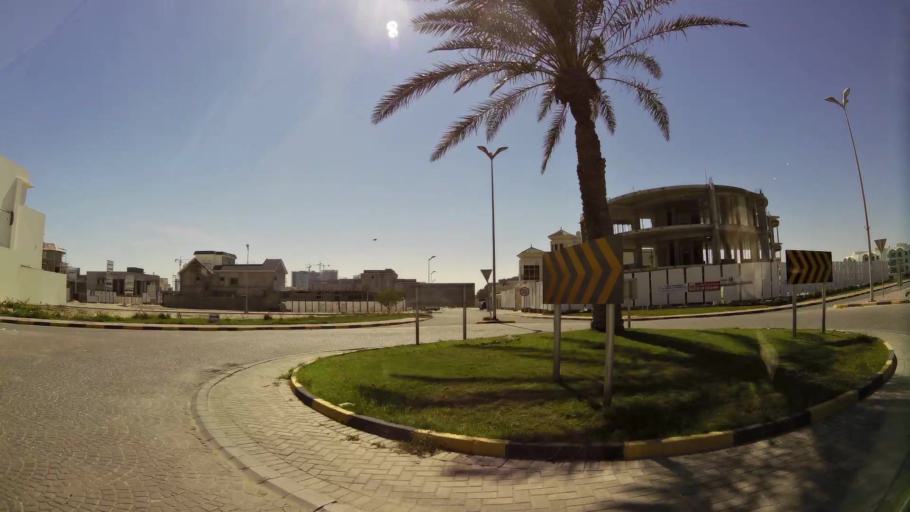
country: BH
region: Muharraq
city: Al Hadd
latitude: 26.2983
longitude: 50.6681
